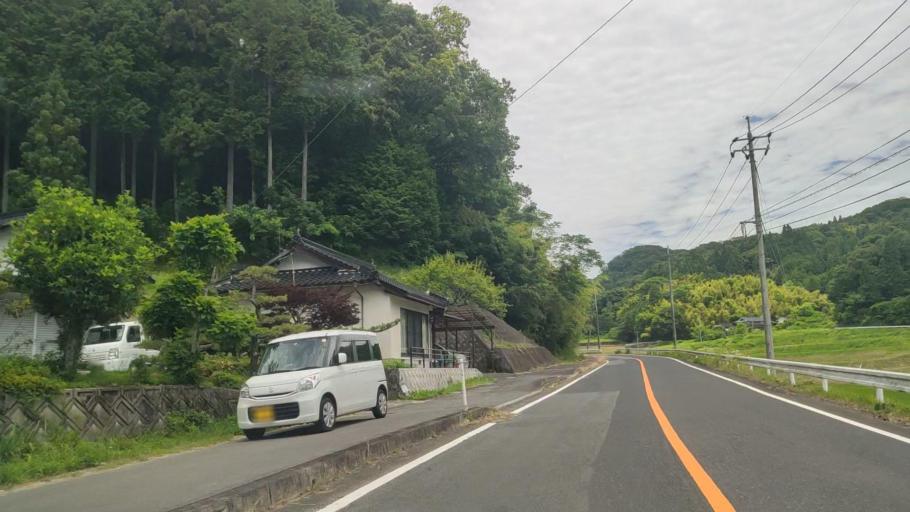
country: JP
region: Okayama
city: Tsuyama
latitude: 35.0869
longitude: 134.2539
